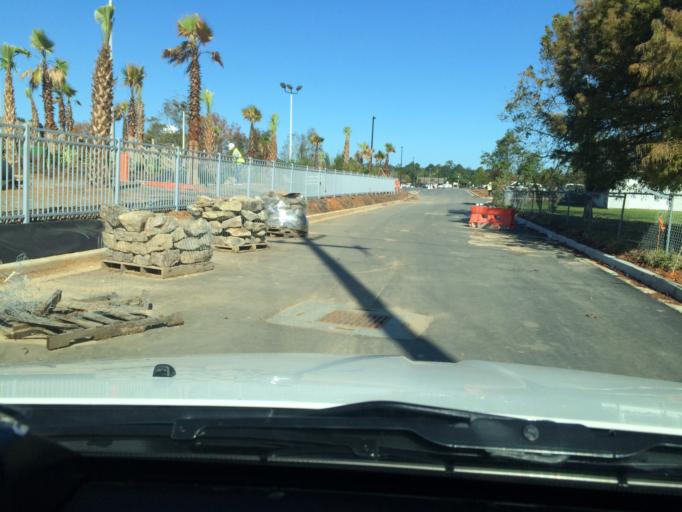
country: US
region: Mississippi
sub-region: Harrison County
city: D'Iberville
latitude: 30.4263
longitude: -88.8892
